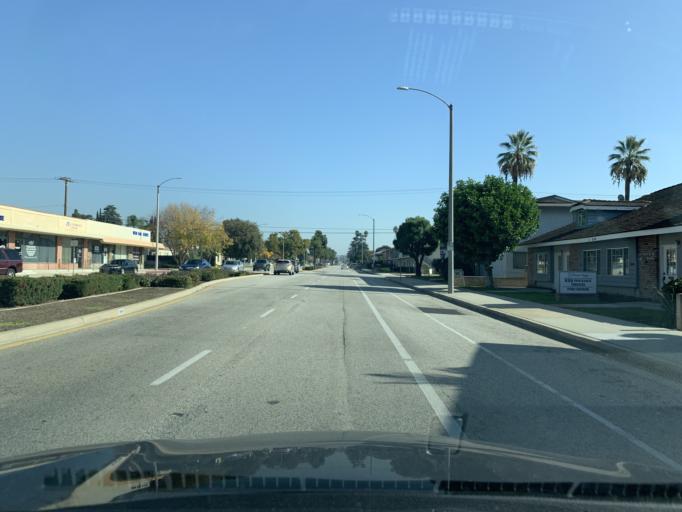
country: US
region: California
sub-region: Los Angeles County
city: Covina
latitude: 34.0862
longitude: -117.8867
